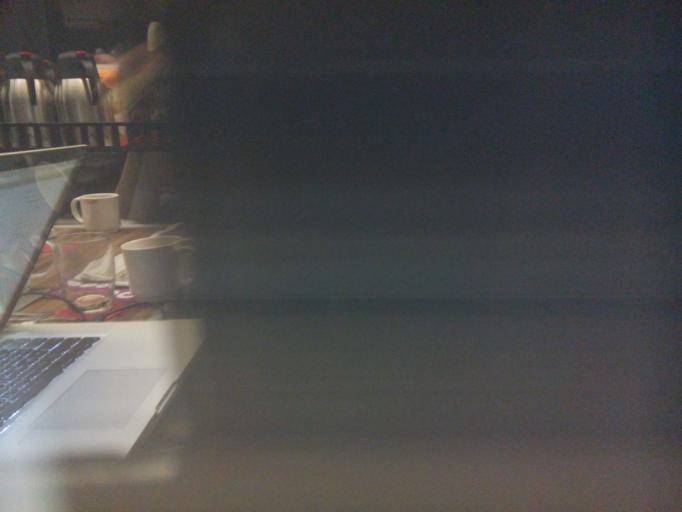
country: GB
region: England
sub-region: Northumberland
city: Cramlington
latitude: 55.0451
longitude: -1.5902
